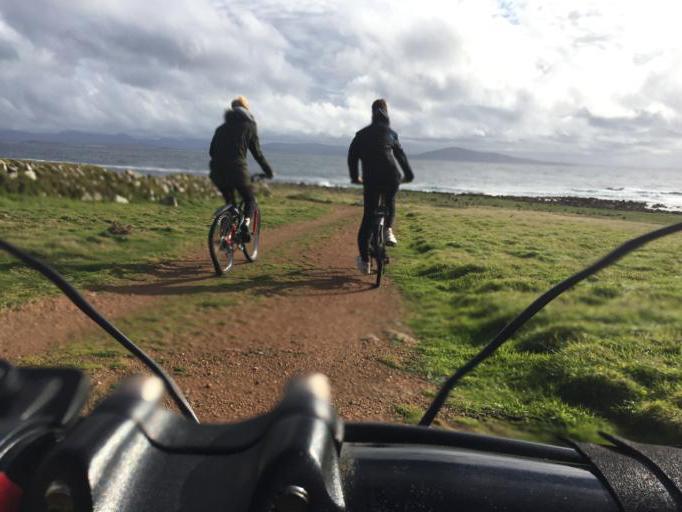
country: IE
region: Ulster
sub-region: County Donegal
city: Derrybeg
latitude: 55.2632
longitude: -8.2343
